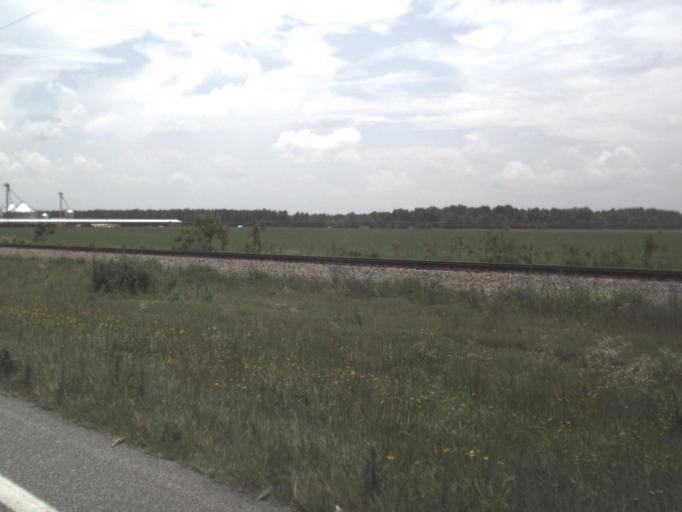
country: US
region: Florida
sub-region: Madison County
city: Madison
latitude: 30.4066
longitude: -83.2462
